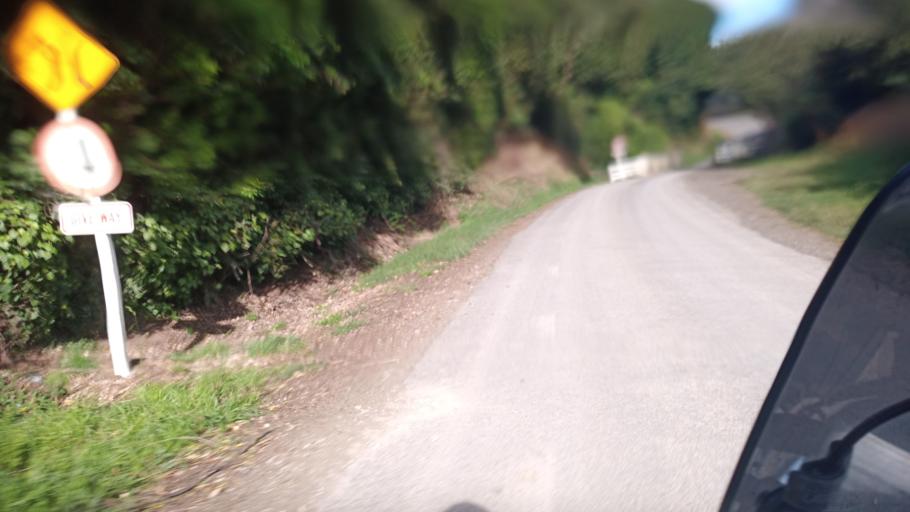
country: NZ
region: Gisborne
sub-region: Gisborne District
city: Gisborne
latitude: -38.5348
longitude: 177.5285
